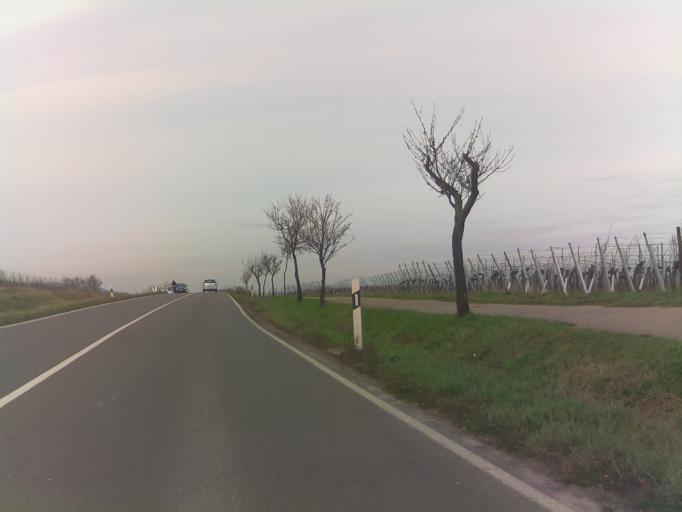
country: DE
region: Rheinland-Pfalz
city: Maikammer
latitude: 49.3081
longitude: 8.1434
